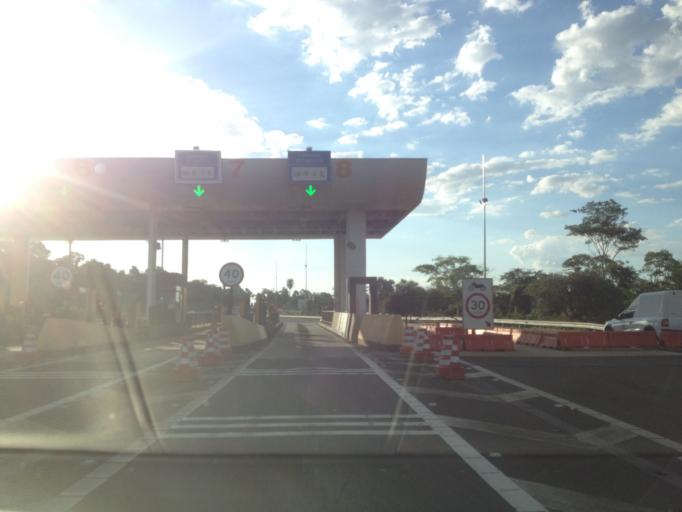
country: BR
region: Sao Paulo
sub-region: Brotas
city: Brotas
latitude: -22.2562
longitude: -48.2434
